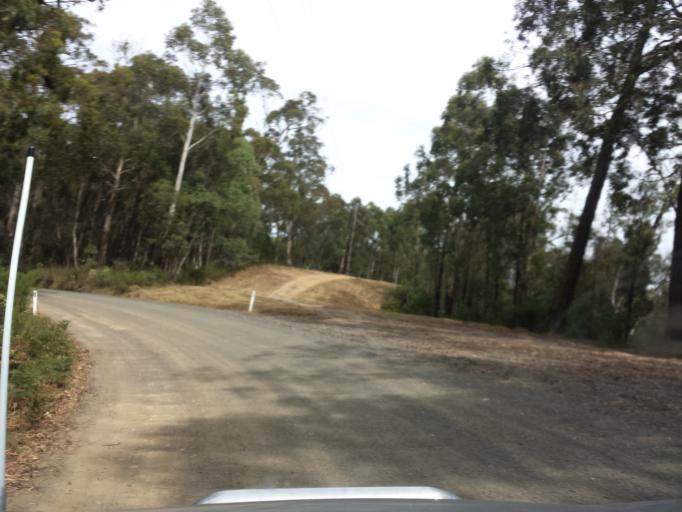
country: AU
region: Victoria
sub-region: Latrobe
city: Moe
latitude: -37.8184
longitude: 146.4034
